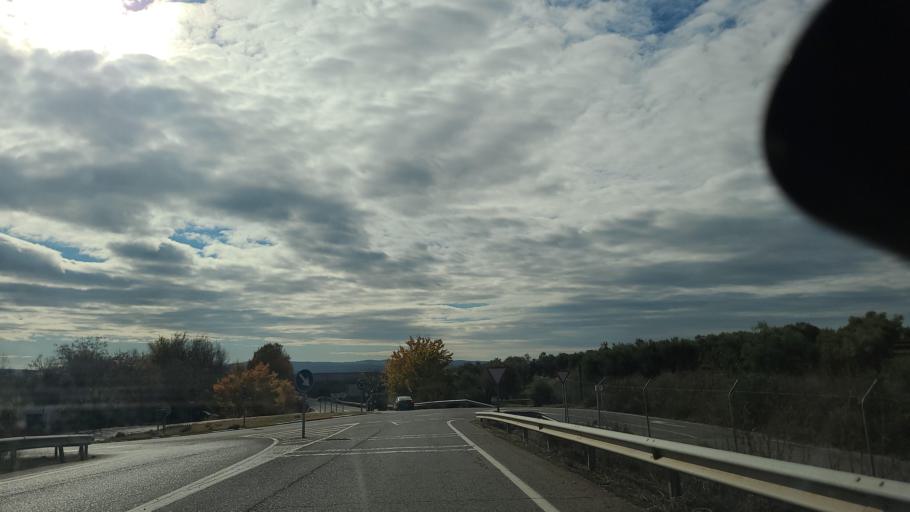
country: ES
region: Andalusia
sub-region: Provincia de Jaen
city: Villanueva de la Reina
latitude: 38.0471
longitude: -3.9090
